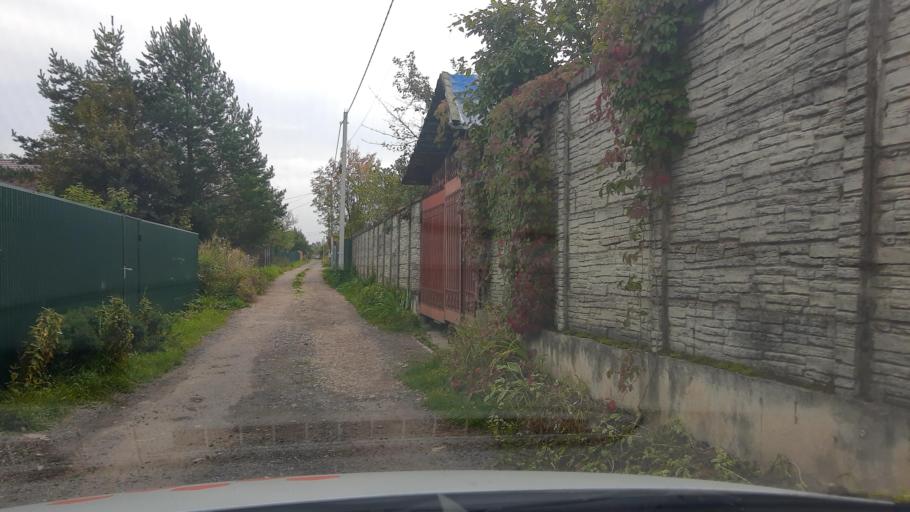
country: RU
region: Moskovskaya
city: Dubrovitsy
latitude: 55.4901
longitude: 37.4874
